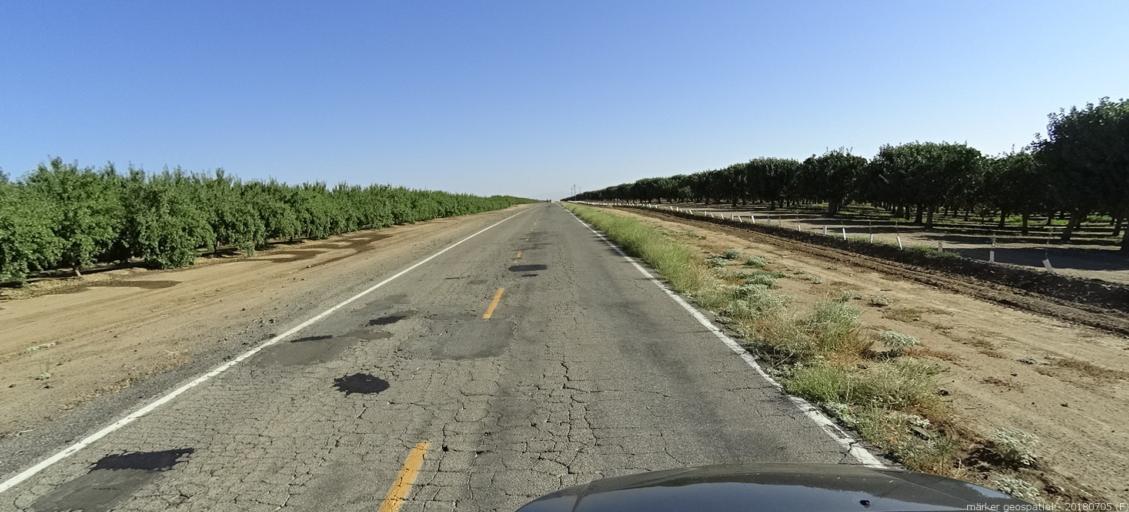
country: US
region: California
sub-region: Madera County
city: Madera Acres
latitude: 37.0998
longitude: -120.0746
